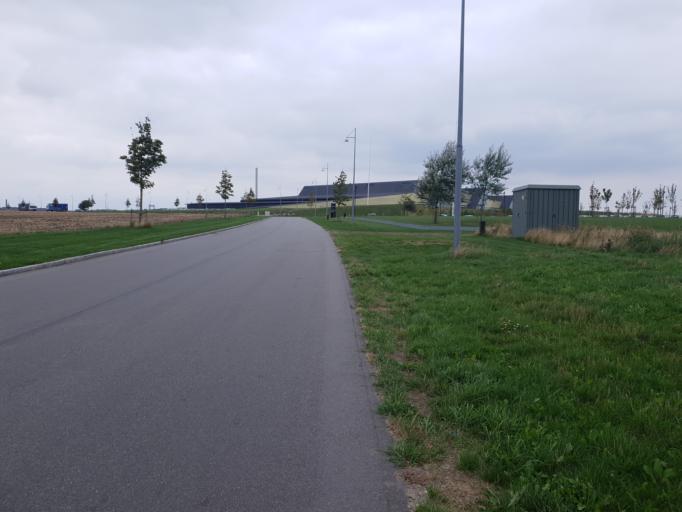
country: DK
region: South Denmark
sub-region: Middelfart Kommune
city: Strib
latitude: 55.5002
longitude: 9.7865
